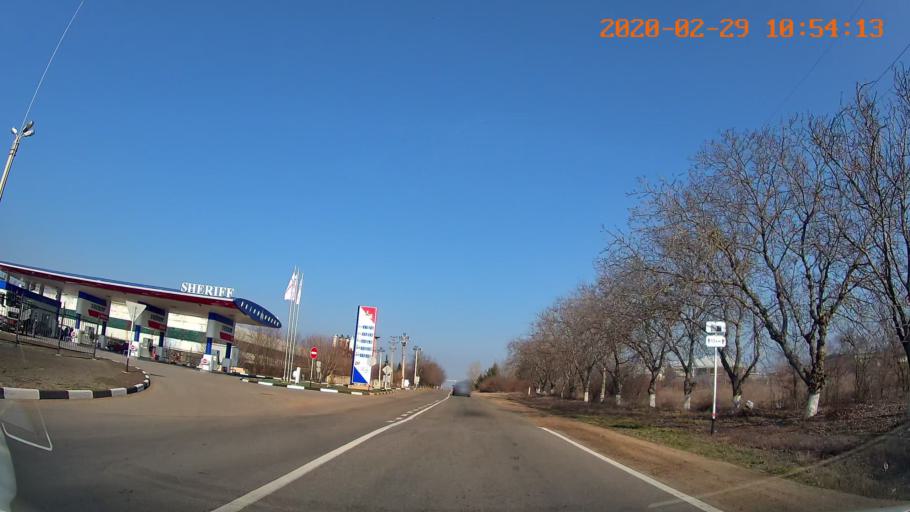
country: MD
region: Telenesti
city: Grigoriopol
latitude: 47.1209
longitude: 29.3278
